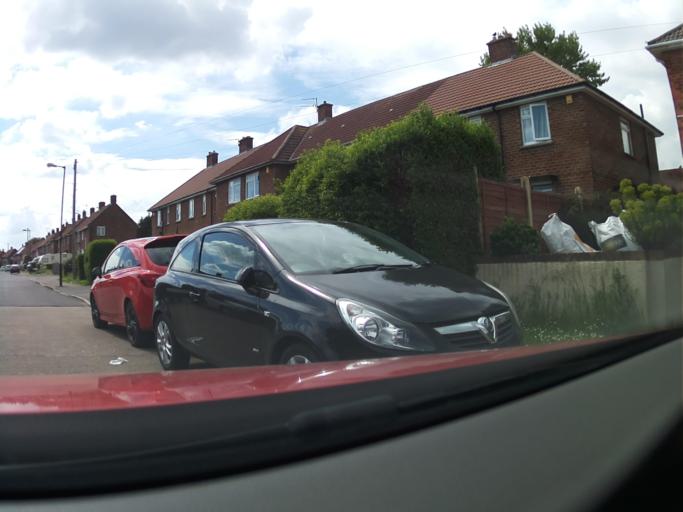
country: GB
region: England
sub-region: Bristol
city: Bristol
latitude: 51.5067
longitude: -2.6054
